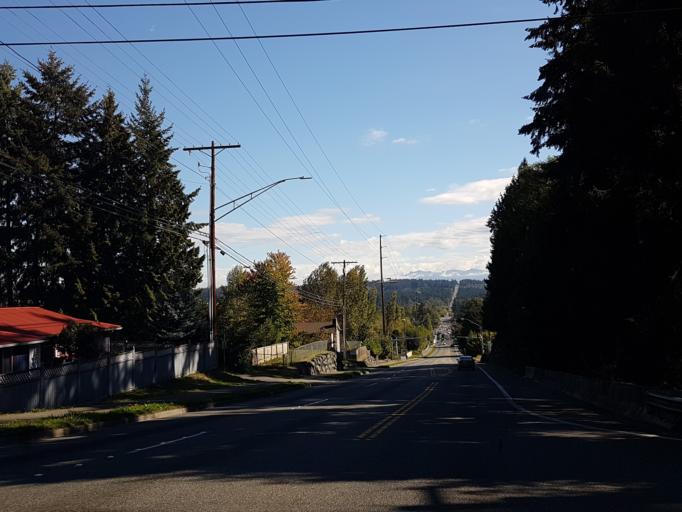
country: US
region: Washington
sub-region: King County
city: Kenmore
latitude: 47.7913
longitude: -122.2289
